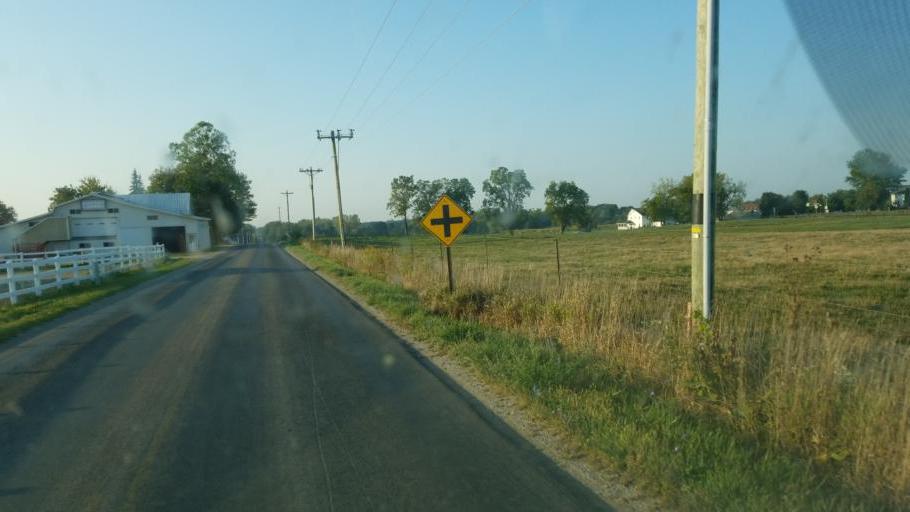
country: US
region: Indiana
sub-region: LaGrange County
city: Lagrange
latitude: 41.5999
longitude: -85.4242
